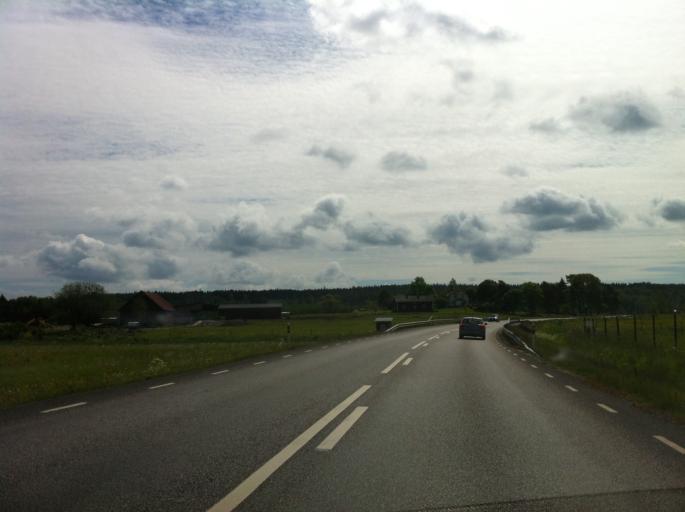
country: SE
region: Vaermland
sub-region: Saffle Kommun
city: Saeffle
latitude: 59.2131
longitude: 13.0190
